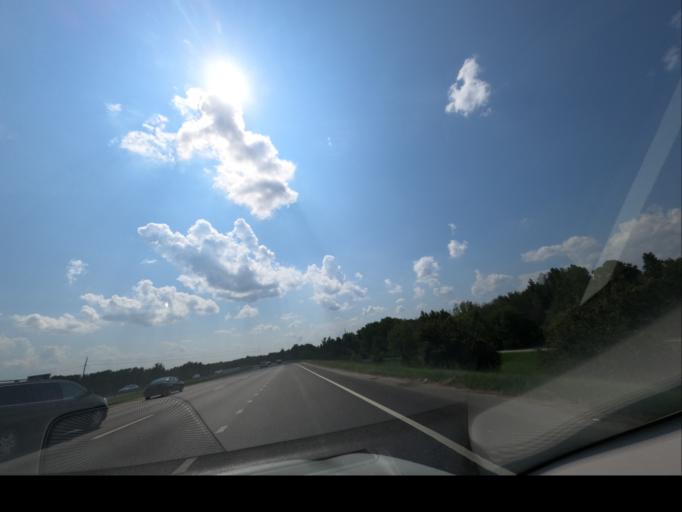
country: US
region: South Carolina
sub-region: Richland County
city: Columbia
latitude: 33.9504
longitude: -80.9907
